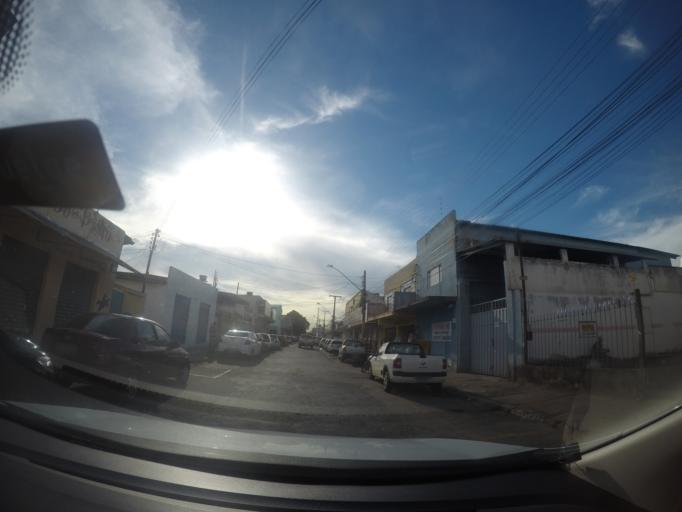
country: BR
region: Goias
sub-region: Goiania
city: Goiania
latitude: -16.6733
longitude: -49.2896
